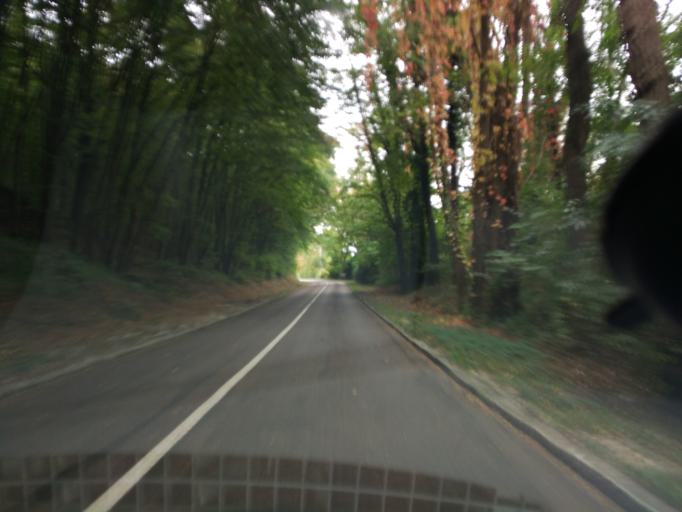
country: FR
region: Ile-de-France
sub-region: Departement de l'Essonne
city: Les Molieres
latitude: 48.6866
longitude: 2.0666
